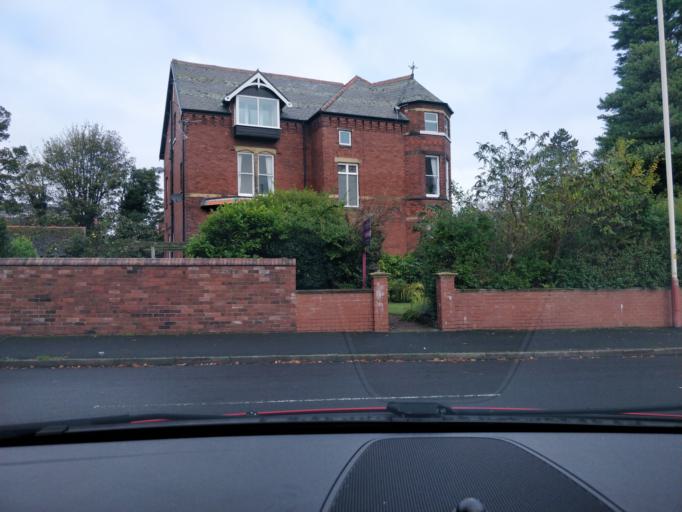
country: GB
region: England
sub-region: Sefton
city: Southport
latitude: 53.6349
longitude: -3.0231
